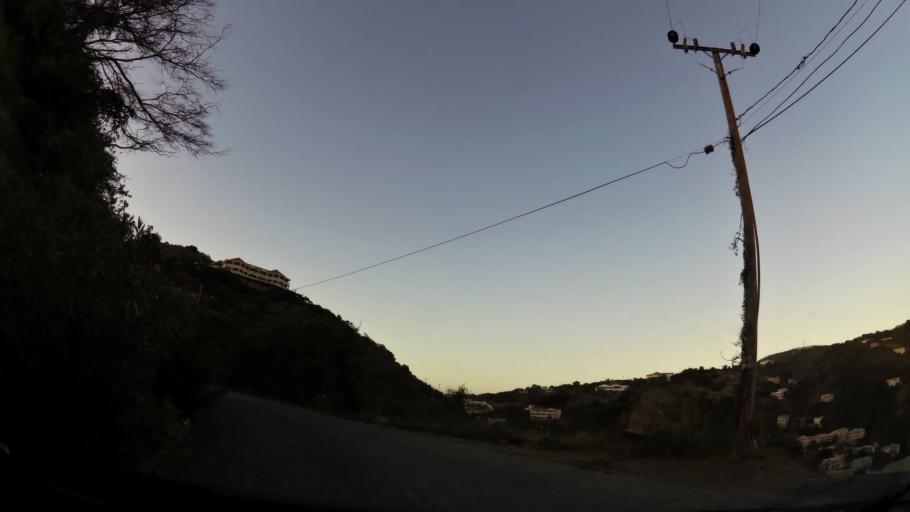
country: VG
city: Tortola
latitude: 18.4438
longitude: -64.5760
